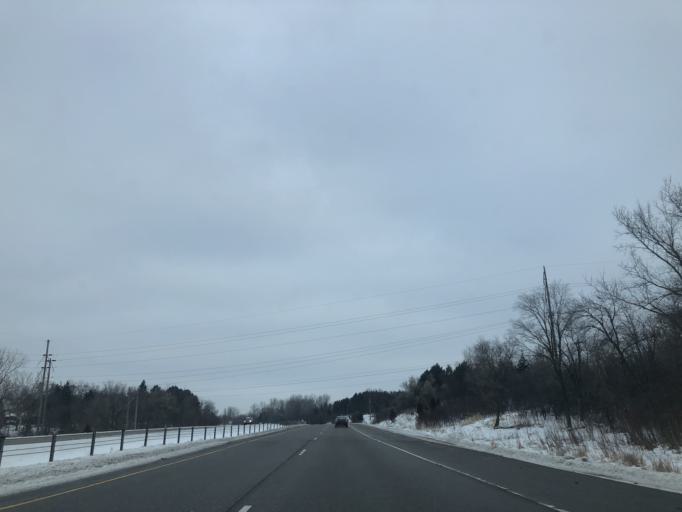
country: US
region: Minnesota
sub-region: Ramsey County
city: Shoreview
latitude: 45.0710
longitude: -93.1683
